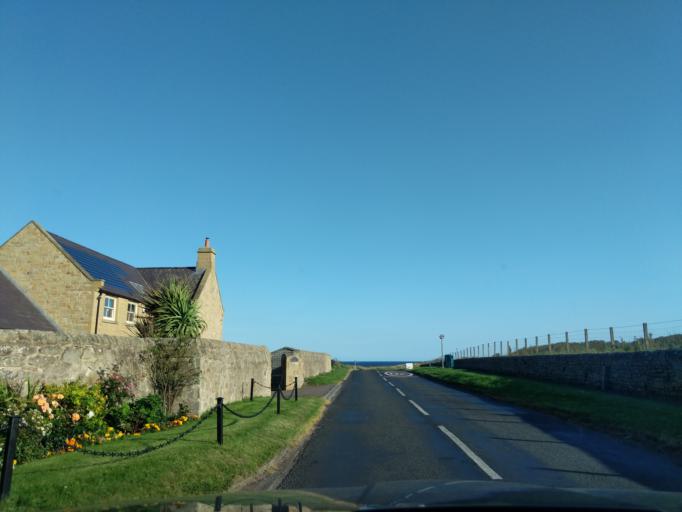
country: GB
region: England
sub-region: Northumberland
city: Lynemouth
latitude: 55.2342
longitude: -1.5365
